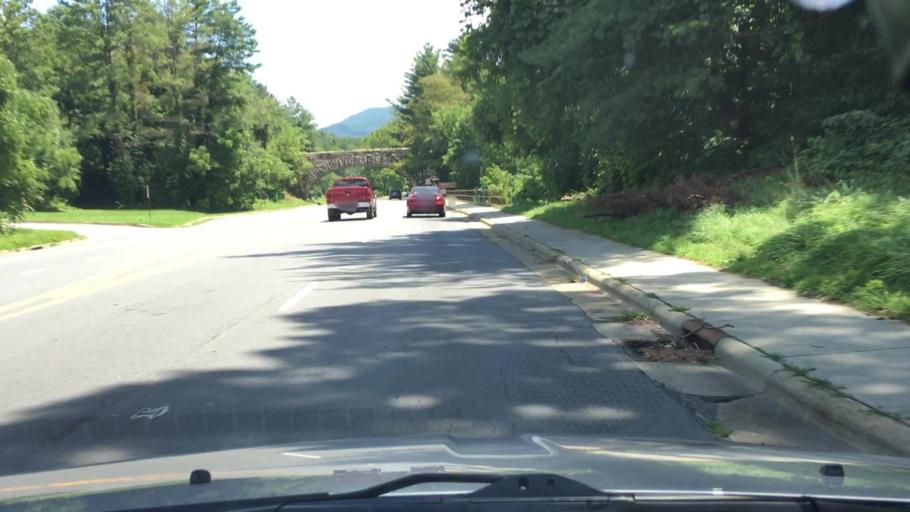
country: US
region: North Carolina
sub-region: Buncombe County
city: Biltmore Forest
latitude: 35.5865
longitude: -82.4812
